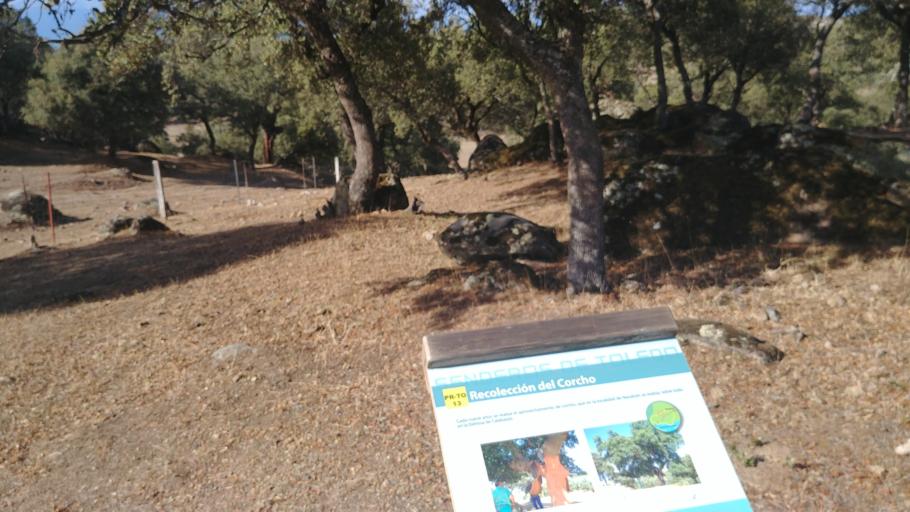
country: ES
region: Castille-La Mancha
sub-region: Province of Toledo
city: Navalcan
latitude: 40.0661
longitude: -5.1194
